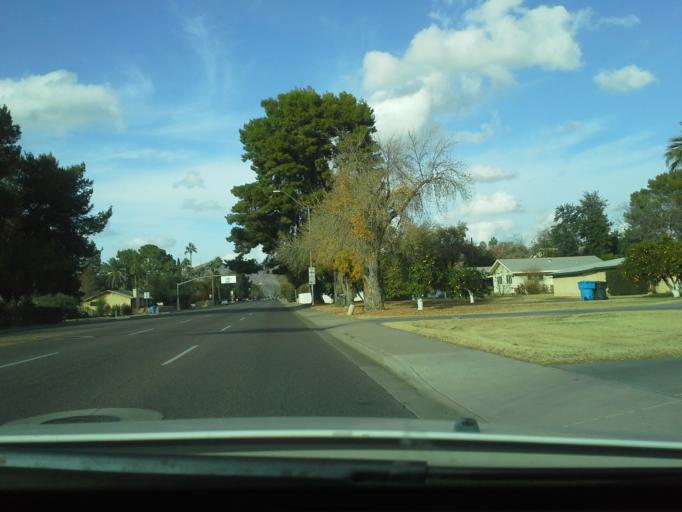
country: US
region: Arizona
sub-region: Maricopa County
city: Glendale
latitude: 33.5540
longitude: -112.0825
